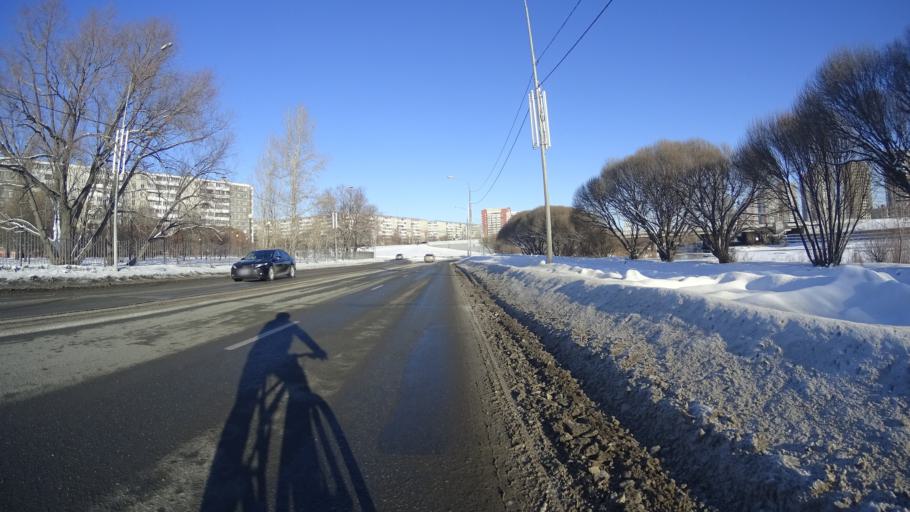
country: RU
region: Chelyabinsk
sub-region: Gorod Chelyabinsk
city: Chelyabinsk
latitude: 55.1745
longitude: 61.3558
